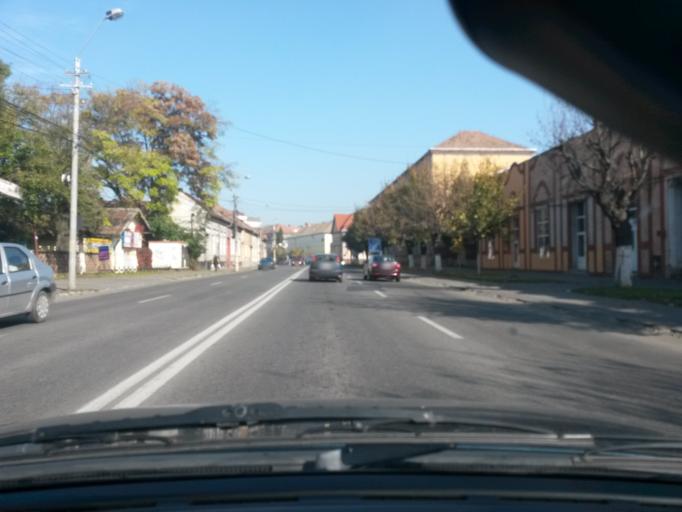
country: RO
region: Mures
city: Targu-Mures
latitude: 46.5364
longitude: 24.5563
